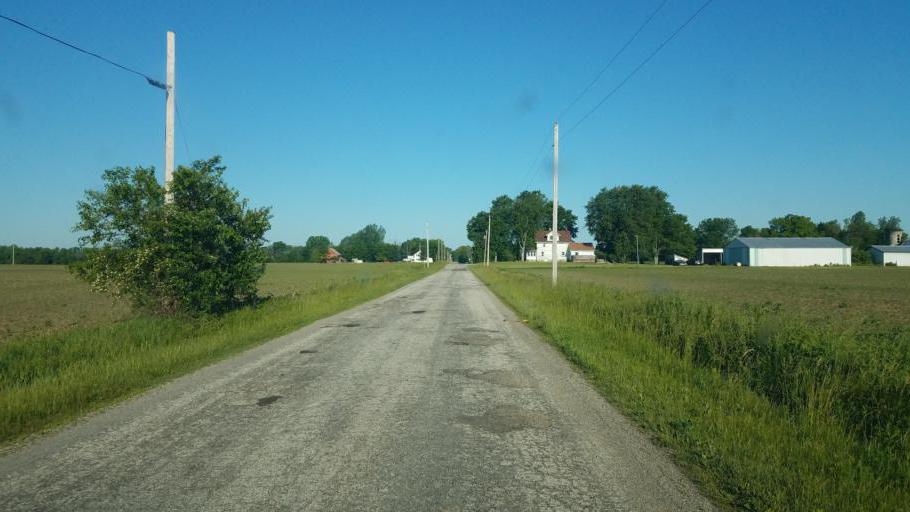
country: US
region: Ohio
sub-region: Morrow County
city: Cardington
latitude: 40.6163
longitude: -82.9345
